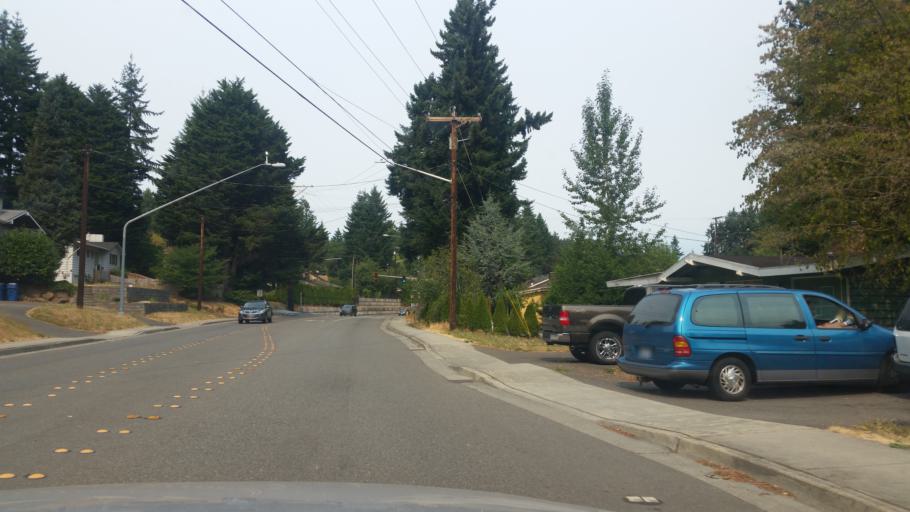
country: US
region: Washington
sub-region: Snohomish County
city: Meadowdale
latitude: 47.8383
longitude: -122.3249
